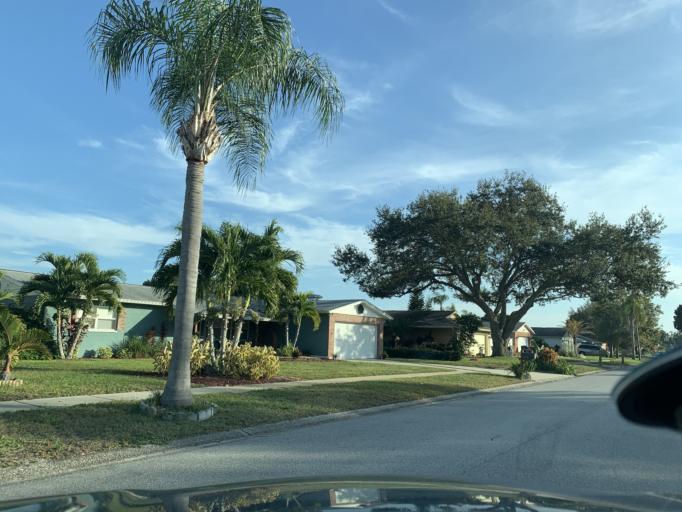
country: US
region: Florida
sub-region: Pinellas County
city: Ridgecrest
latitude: 27.8926
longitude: -82.7960
